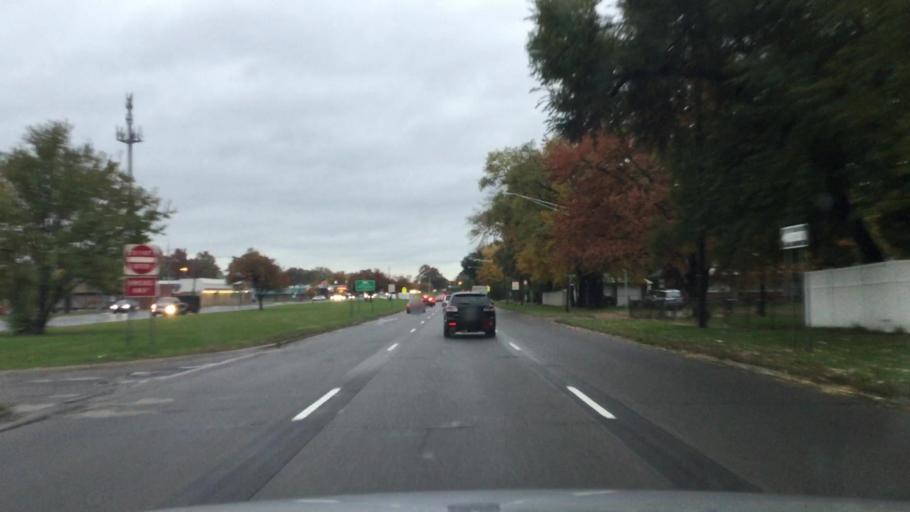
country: US
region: Michigan
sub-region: Wayne County
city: Inkster
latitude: 42.2913
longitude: -83.2716
